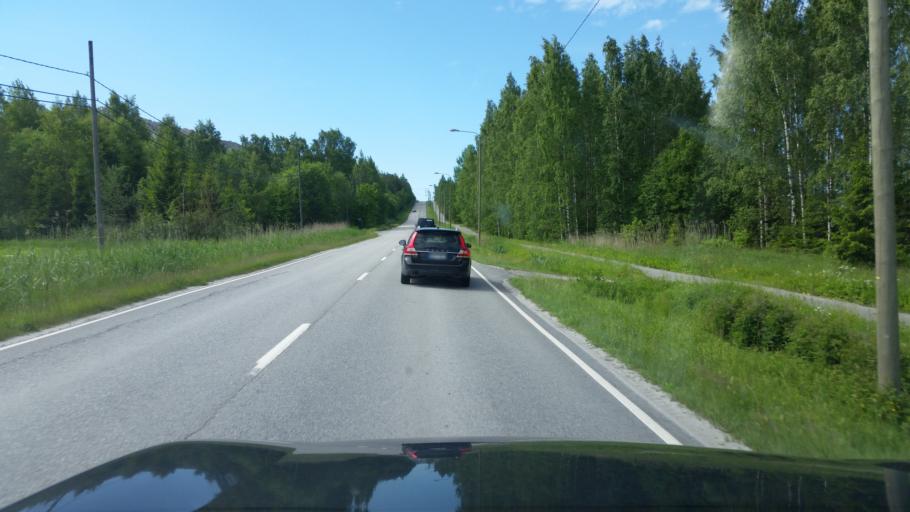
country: FI
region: Varsinais-Suomi
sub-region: Aboland-Turunmaa
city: Laensi-Turunmaa
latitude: 60.2951
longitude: 22.2687
